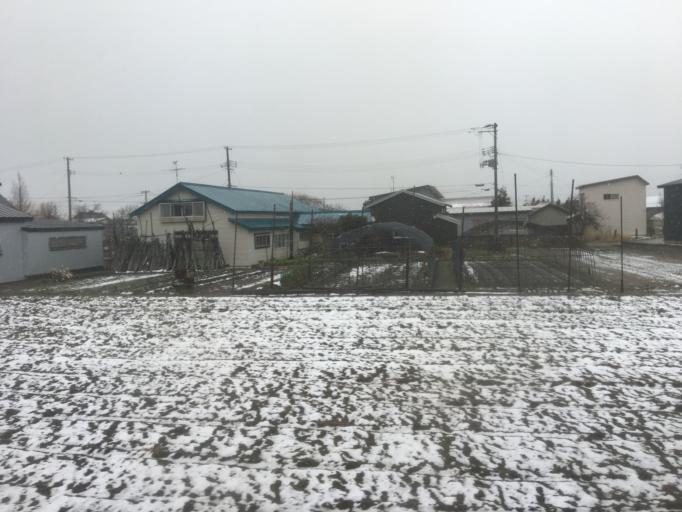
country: JP
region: Aomori
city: Aomori Shi
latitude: 40.9158
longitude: 140.6667
